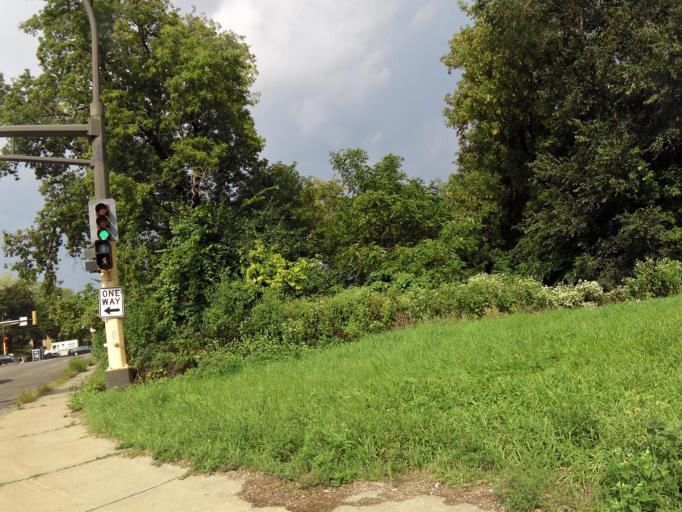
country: US
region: Minnesota
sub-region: Dakota County
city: Mendota Heights
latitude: 44.9270
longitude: -93.1455
